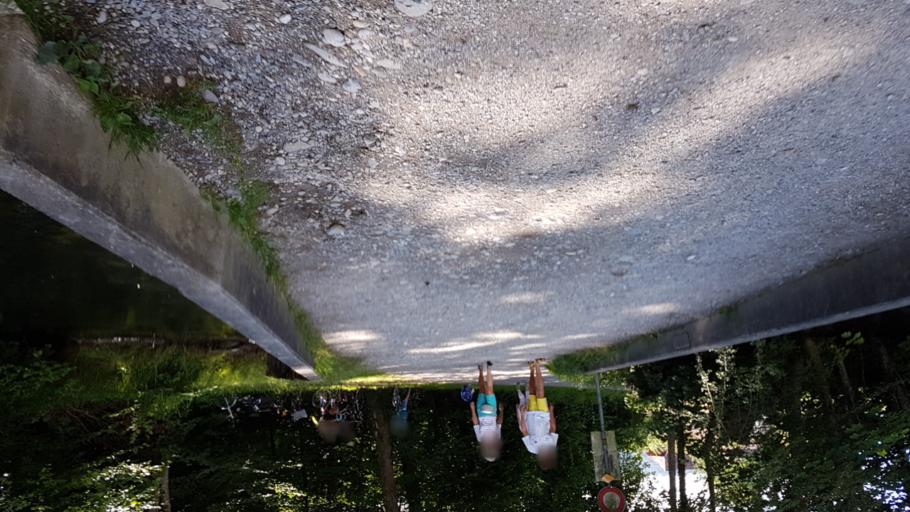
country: CH
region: Bern
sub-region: Bern-Mittelland District
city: Muri
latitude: 46.9181
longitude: 7.5001
